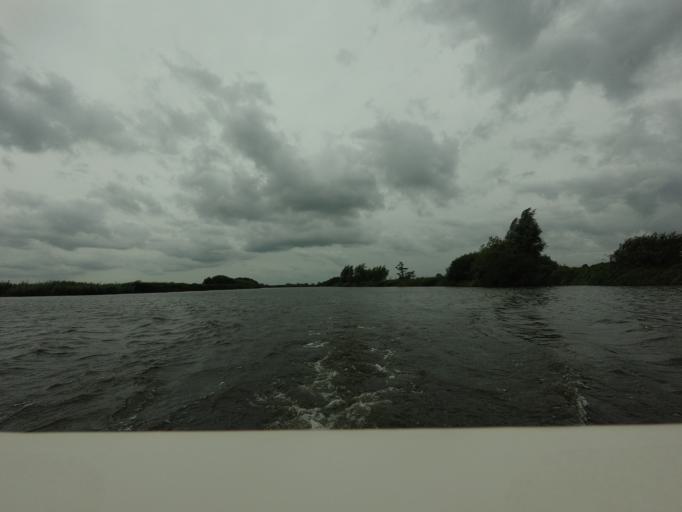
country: NL
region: Friesland
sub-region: Gemeente Boarnsterhim
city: Warten
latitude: 53.1012
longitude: 5.9091
